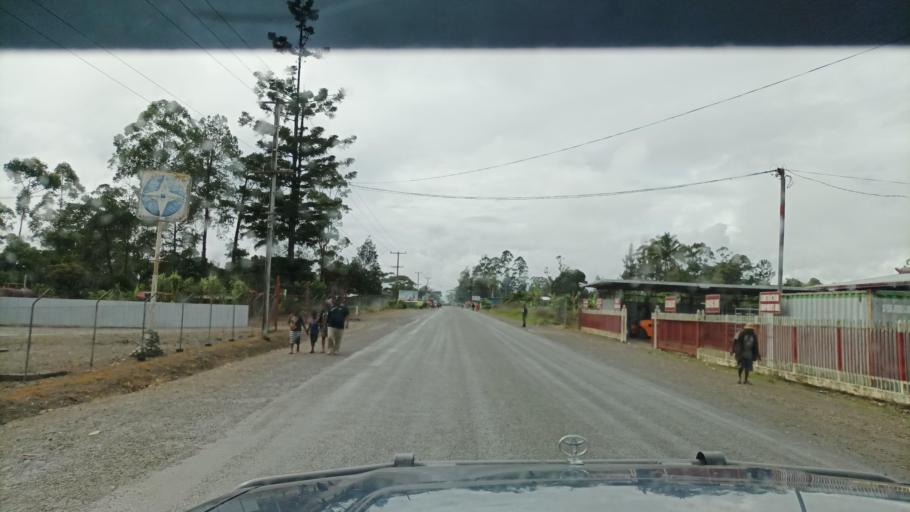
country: PG
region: Jiwaka
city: Minj
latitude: -5.8790
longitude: 144.6752
